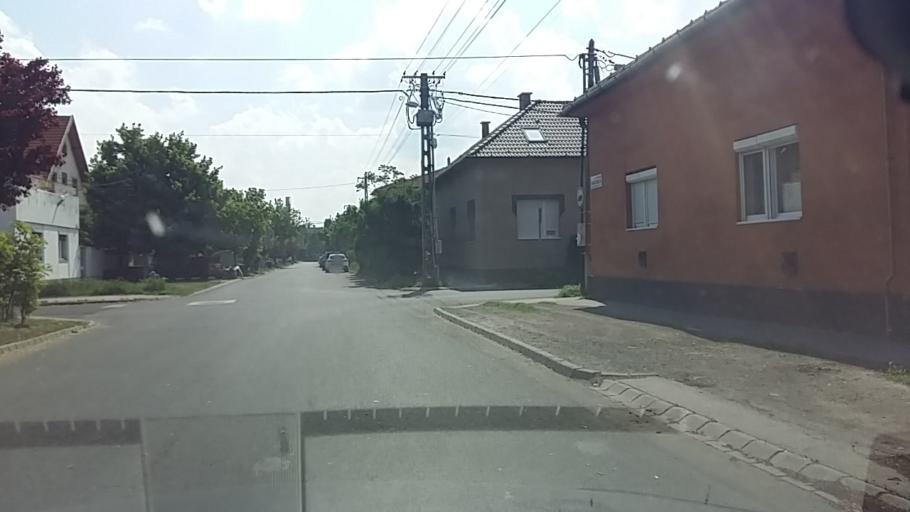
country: HU
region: Budapest
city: Budapest XV. keruelet
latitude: 47.5595
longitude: 19.1277
